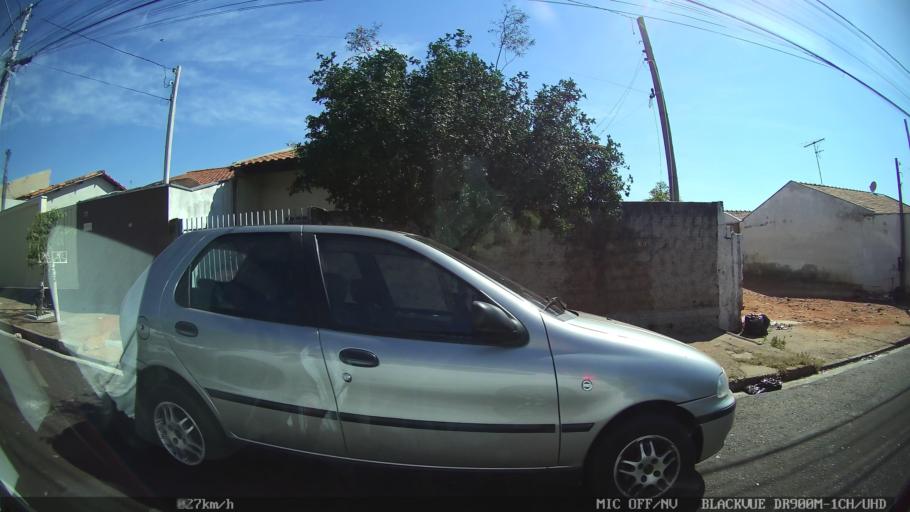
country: BR
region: Sao Paulo
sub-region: Sao Jose Do Rio Preto
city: Sao Jose do Rio Preto
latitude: -20.7756
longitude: -49.4052
